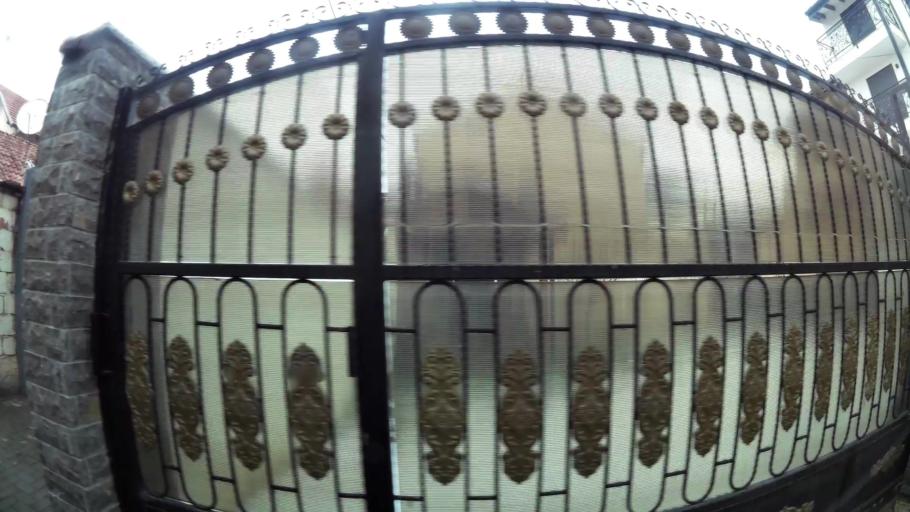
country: XK
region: Pristina
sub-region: Komuna e Prishtines
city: Pristina
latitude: 42.6727
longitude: 21.1705
